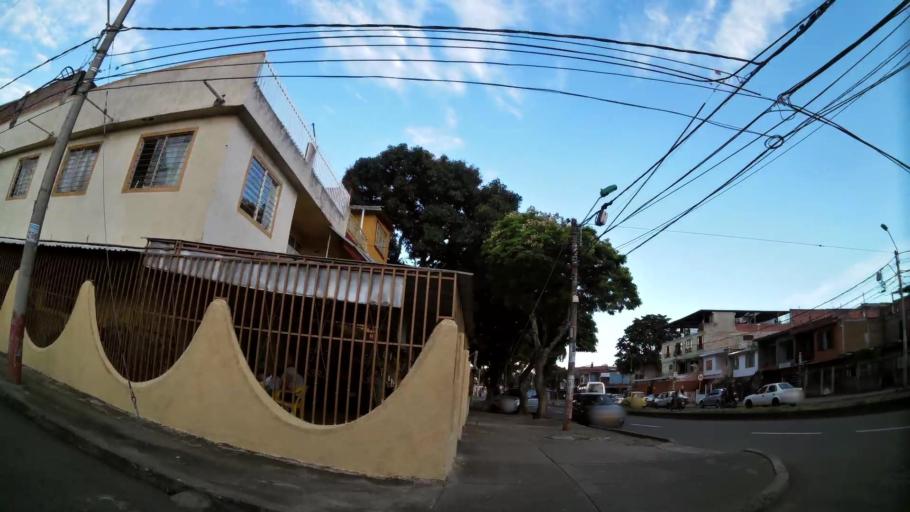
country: CO
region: Valle del Cauca
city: Cali
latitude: 3.4243
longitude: -76.5070
